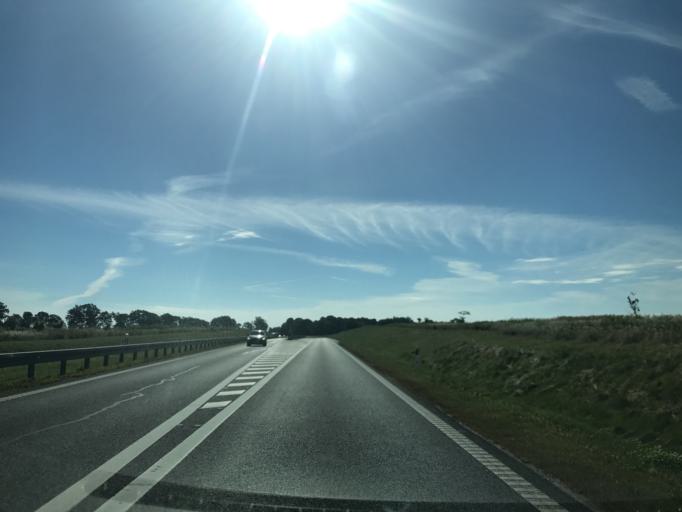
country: PL
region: Pomeranian Voivodeship
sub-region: Powiat chojnicki
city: Chojnice
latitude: 53.6801
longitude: 17.5714
